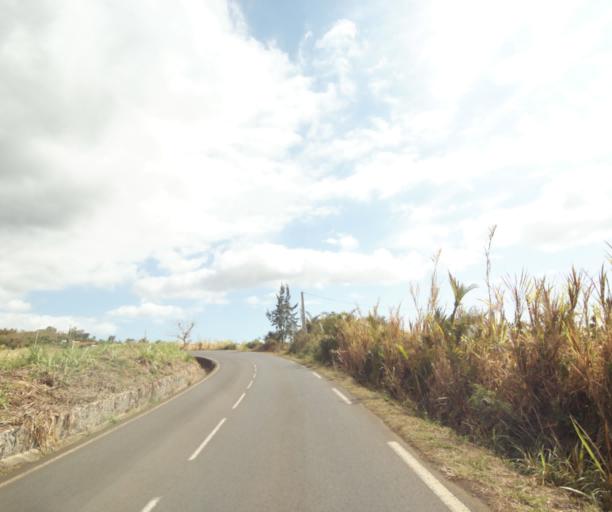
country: RE
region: Reunion
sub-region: Reunion
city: Saint-Paul
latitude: -21.0321
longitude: 55.2863
